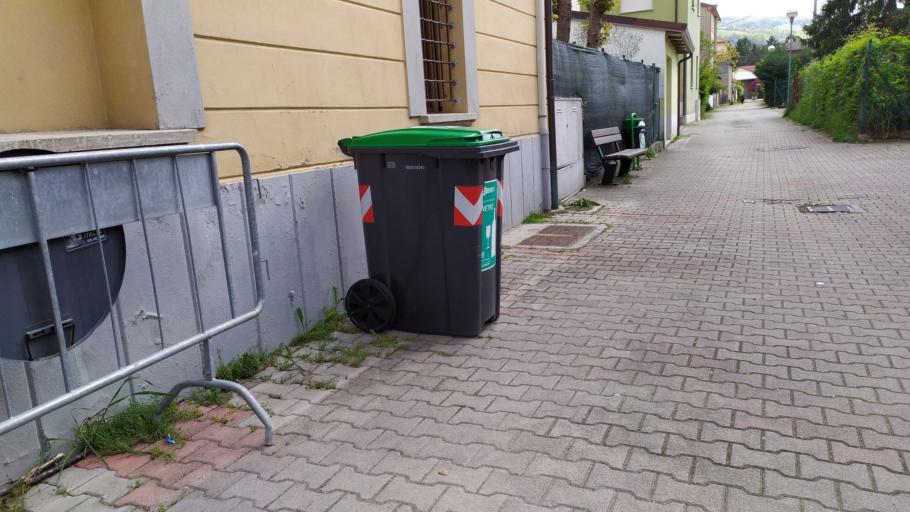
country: IT
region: Emilia-Romagna
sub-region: Provincia di Bologna
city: Borgo Tossignano
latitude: 44.2773
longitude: 11.5880
